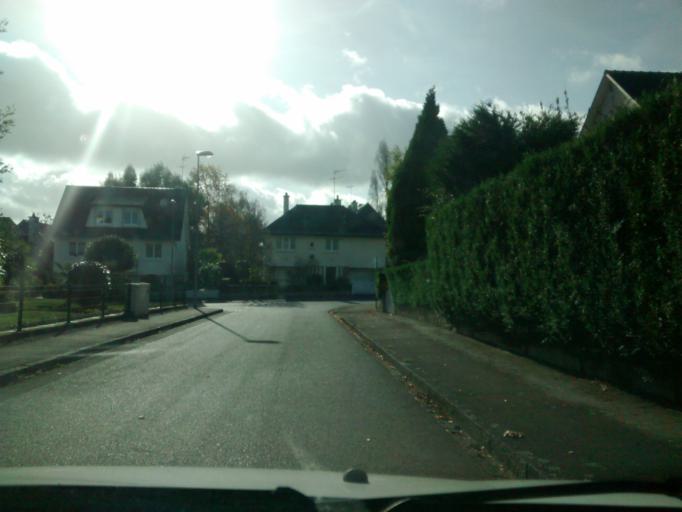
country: FR
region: Brittany
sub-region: Departement d'Ille-et-Vilaine
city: Cesson-Sevigne
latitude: 48.1200
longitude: -1.6113
